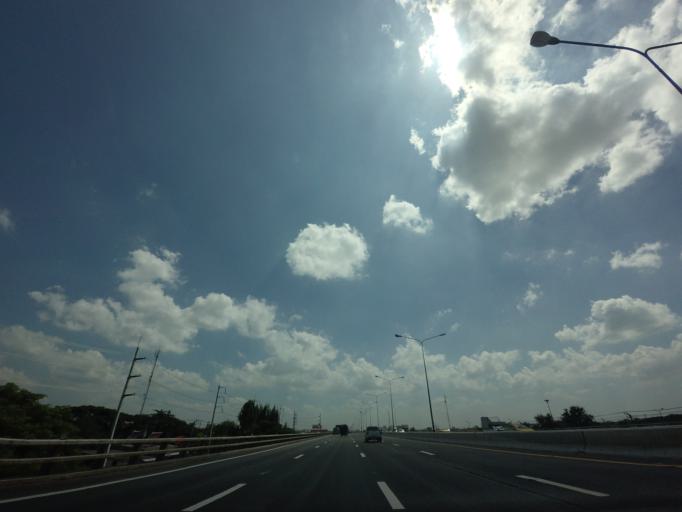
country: TH
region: Bangkok
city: Lat Krabang
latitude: 13.7128
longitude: 100.8189
